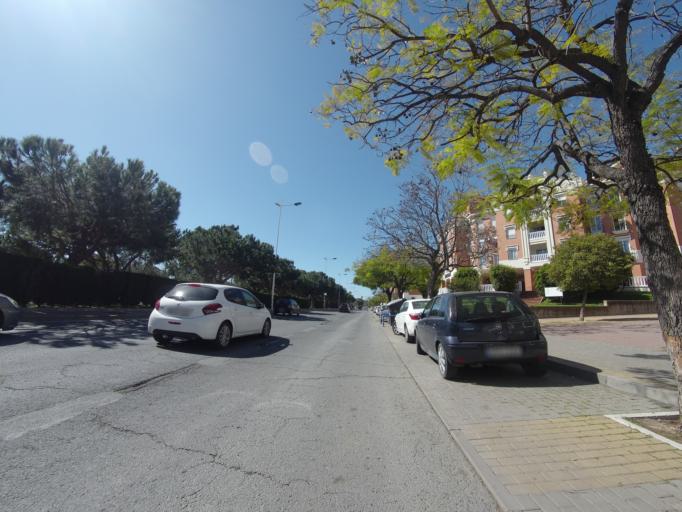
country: ES
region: Andalusia
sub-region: Provincia de Huelva
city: Huelva
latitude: 37.2686
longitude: -6.9347
